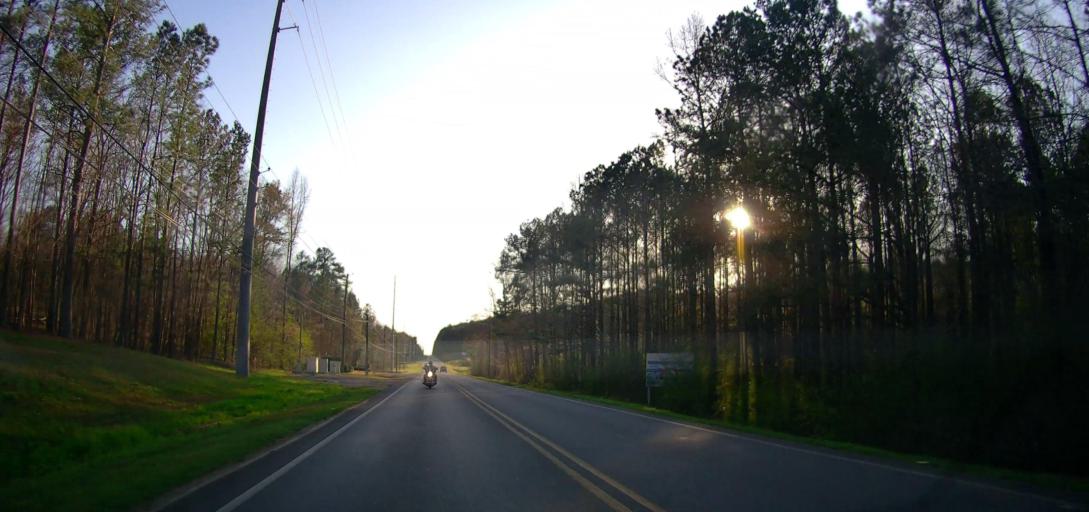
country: US
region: Alabama
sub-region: Shelby County
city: Chelsea
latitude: 33.3430
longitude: -86.6688
